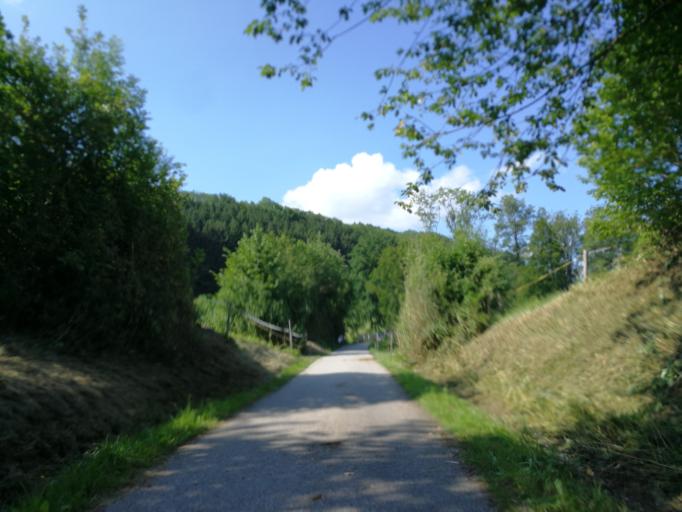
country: AT
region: Salzburg
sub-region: Politischer Bezirk Salzburg-Umgebung
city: Hallwang
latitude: 47.8361
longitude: 13.0768
